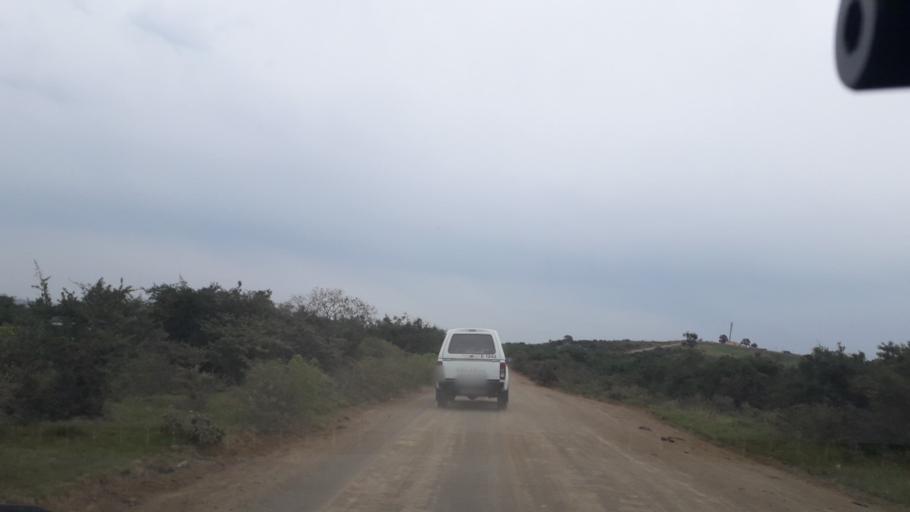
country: ZA
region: Eastern Cape
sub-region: Buffalo City Metropolitan Municipality
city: Bhisho
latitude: -32.7908
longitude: 27.3346
